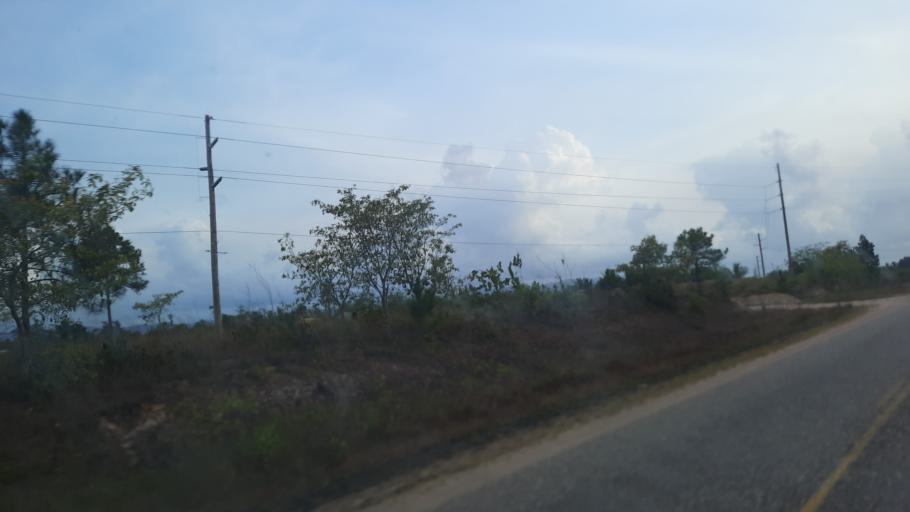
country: BZ
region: Stann Creek
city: Placencia
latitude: 16.6130
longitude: -88.5036
